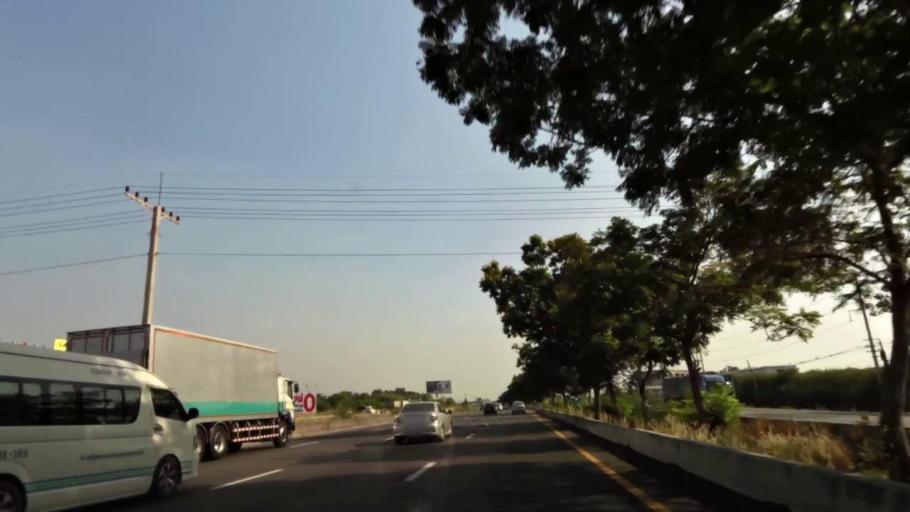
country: TH
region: Ang Thong
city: Ang Thong
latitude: 14.5773
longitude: 100.4864
